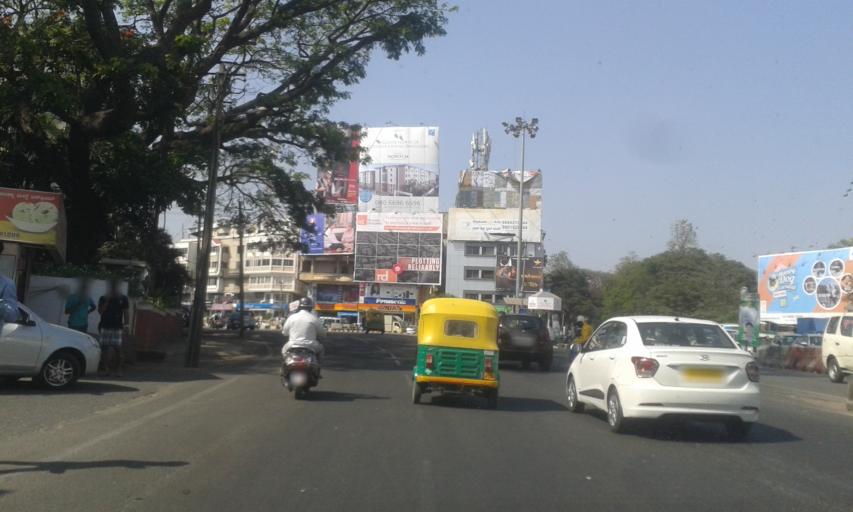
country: IN
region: Karnataka
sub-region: Bangalore Urban
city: Bangalore
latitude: 13.0026
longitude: 77.5840
